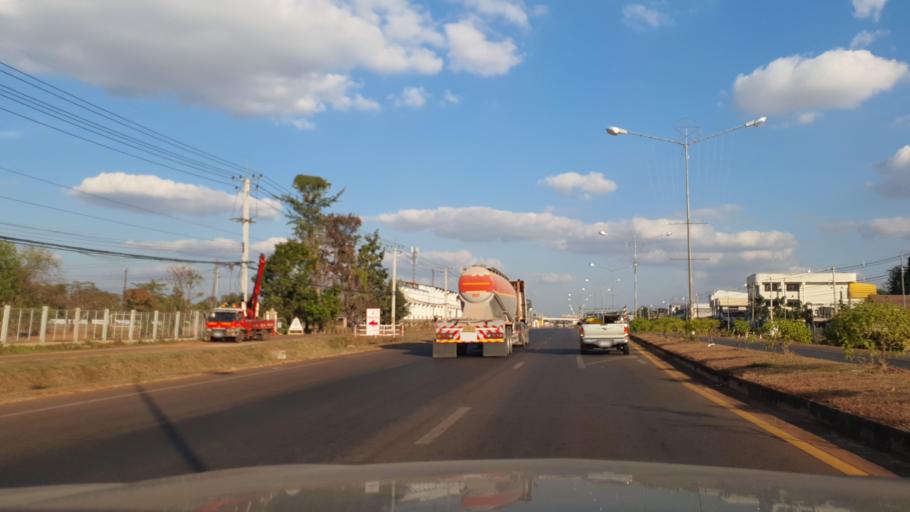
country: TH
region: Sakon Nakhon
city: Sakon Nakhon
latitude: 17.2564
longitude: 104.1784
